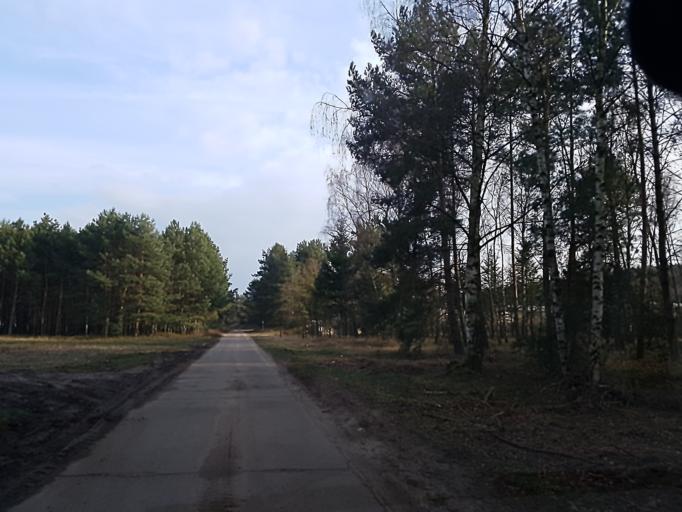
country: DE
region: Brandenburg
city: Wollin
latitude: 52.2704
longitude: 12.4911
